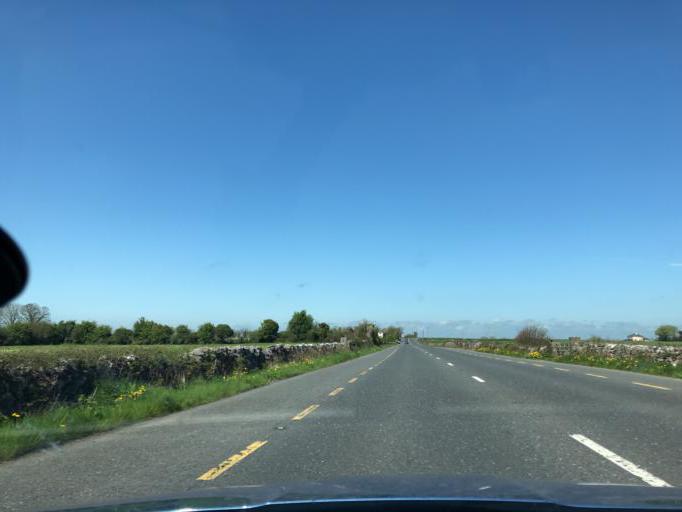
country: IE
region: Connaught
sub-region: County Galway
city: Athenry
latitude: 53.2425
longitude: -8.7570
